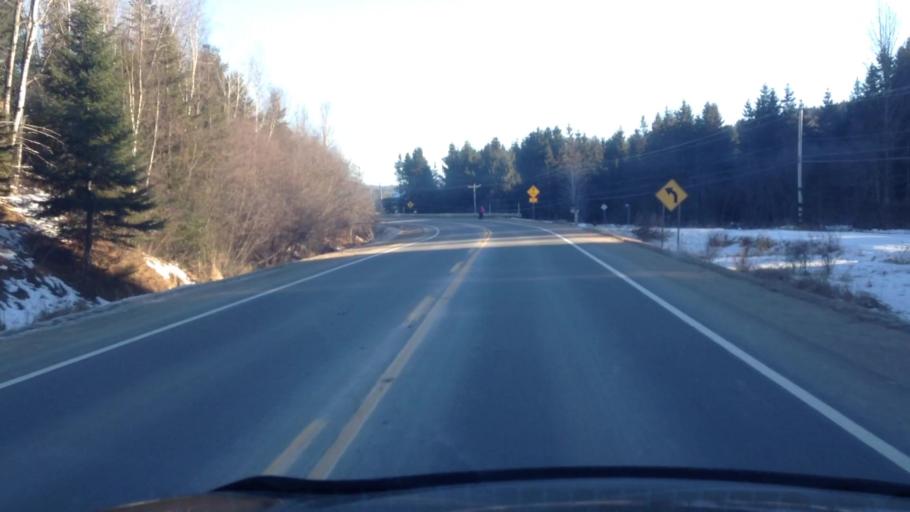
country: CA
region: Quebec
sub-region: Laurentides
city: Mont-Tremblant
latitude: 45.9619
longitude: -74.6063
